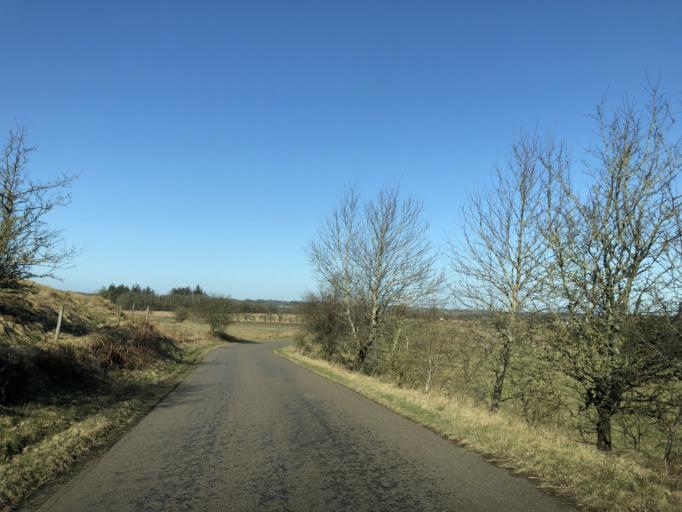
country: DK
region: North Denmark
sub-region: Vesthimmerland Kommune
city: Alestrup
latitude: 56.5665
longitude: 9.4934
